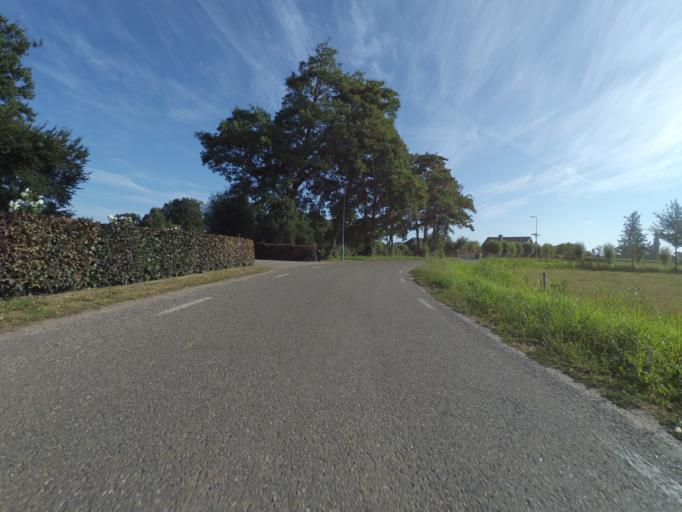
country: NL
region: Gelderland
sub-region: Gemeente Nunspeet
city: Nunspeet
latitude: 52.4105
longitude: 5.7777
